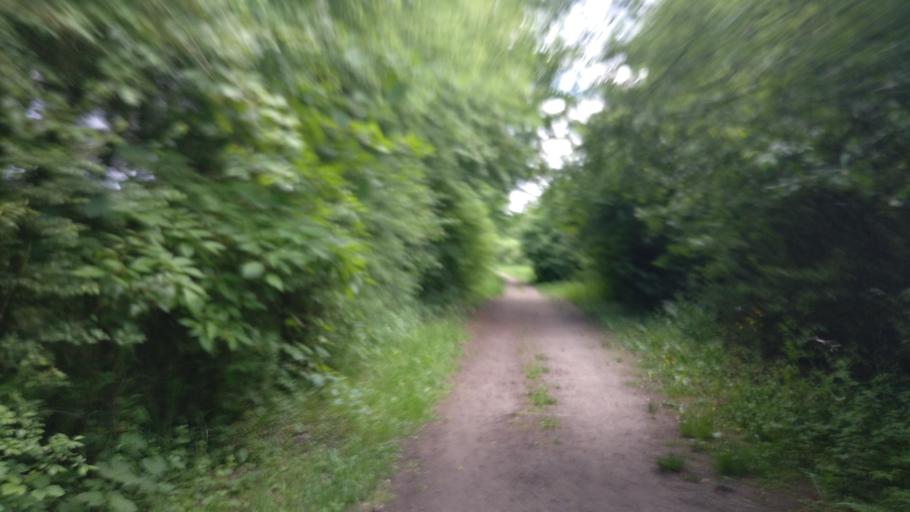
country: DE
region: North Rhine-Westphalia
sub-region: Regierungsbezirk Detmold
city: Lage
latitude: 51.9997
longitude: 8.7765
